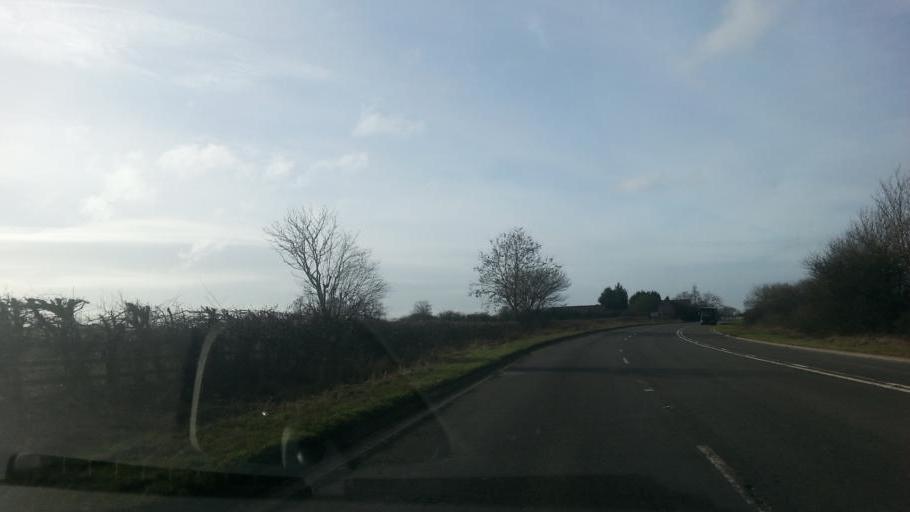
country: GB
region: England
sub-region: District of Rutland
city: Ridlington
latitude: 52.5946
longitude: -0.8256
